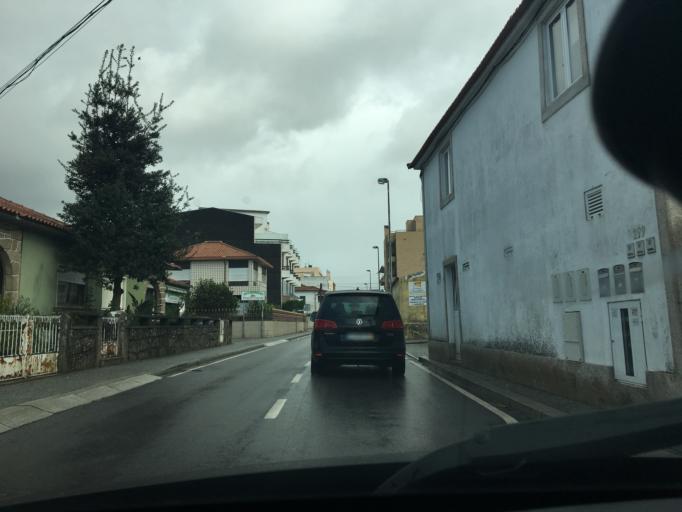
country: PT
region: Porto
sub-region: Matosinhos
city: Santa Cruz do Bispo
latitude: 41.2434
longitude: -8.6657
